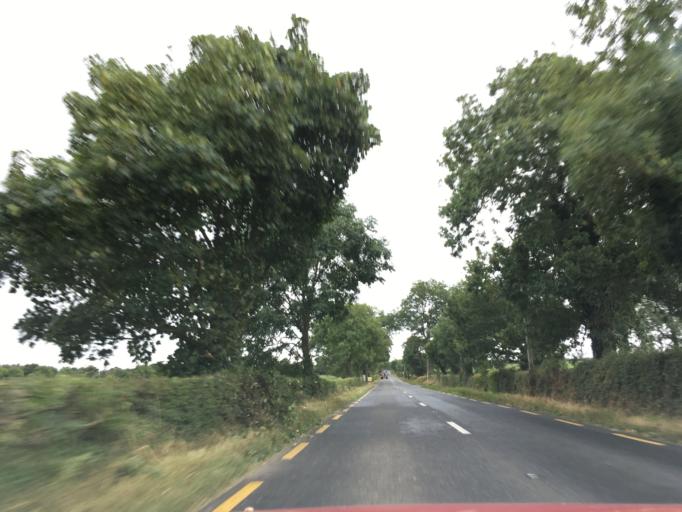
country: IE
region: Munster
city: Fethard
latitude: 52.4361
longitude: -7.7907
